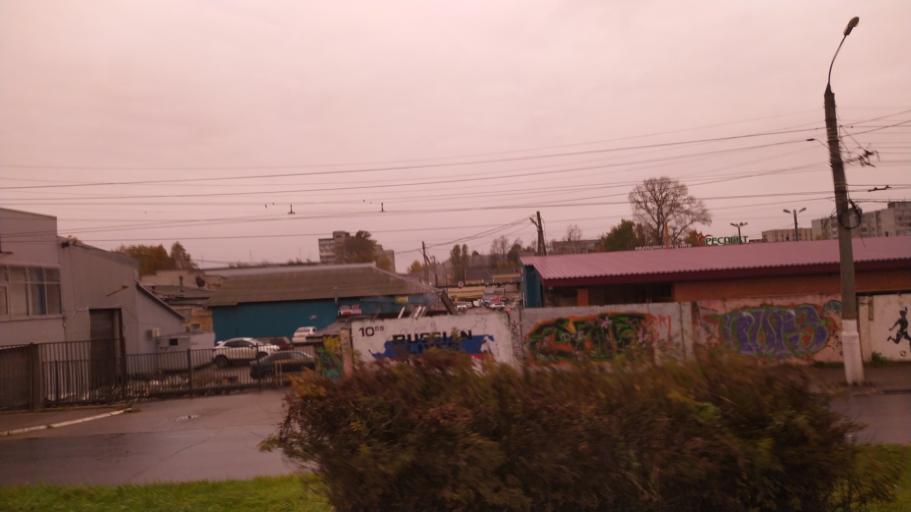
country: RU
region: Tverskaya
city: Tver
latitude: 56.8341
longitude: 35.9047
